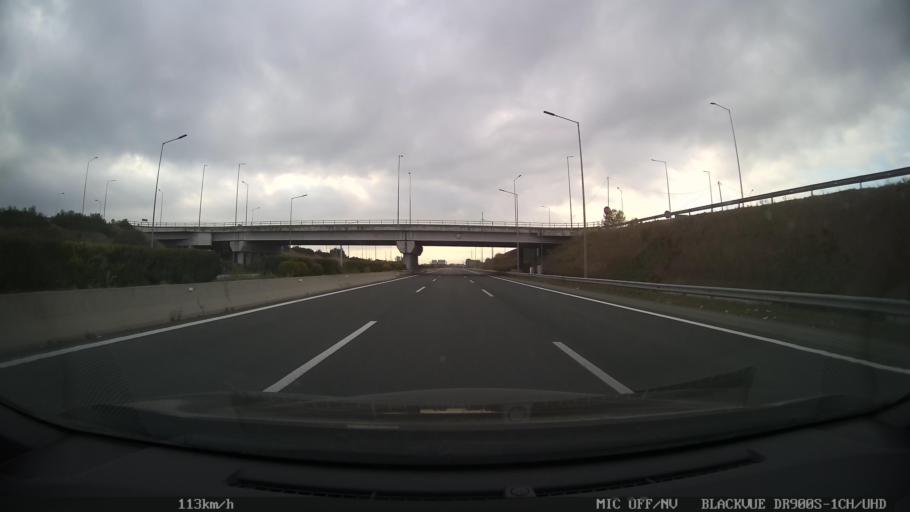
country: GR
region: Central Macedonia
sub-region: Nomos Pierias
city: Nea Efesos
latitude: 40.1942
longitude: 22.5489
